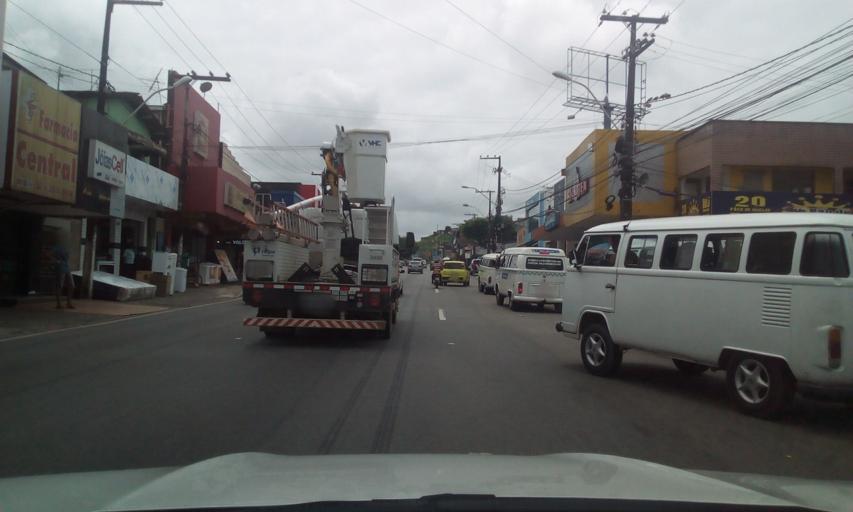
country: BR
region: Pernambuco
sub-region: Abreu E Lima
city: Abreu e Lima
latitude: -7.9049
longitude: -34.9014
